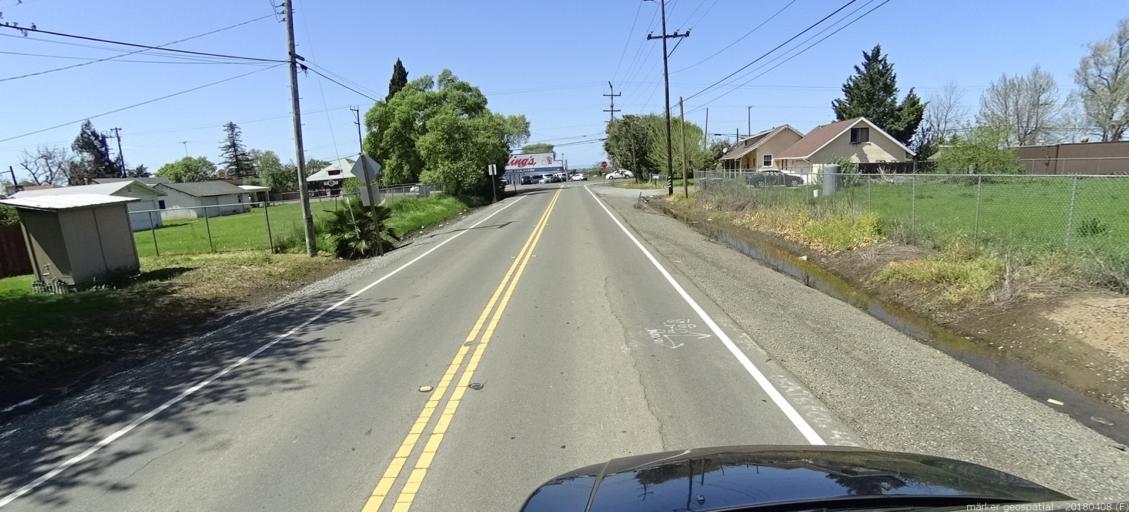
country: US
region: California
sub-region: Sacramento County
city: Laguna
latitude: 38.3792
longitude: -121.4535
